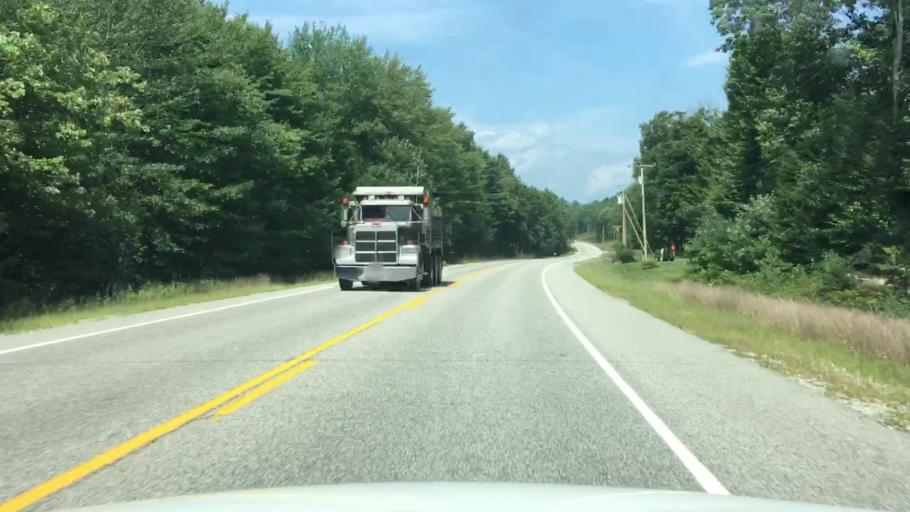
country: US
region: Maine
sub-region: Oxford County
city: Canton
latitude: 44.4738
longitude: -70.3266
